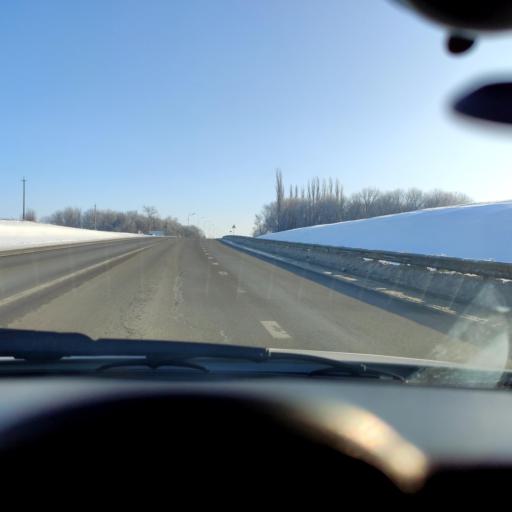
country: RU
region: Kursk
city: Tim
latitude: 51.6555
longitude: 36.9097
